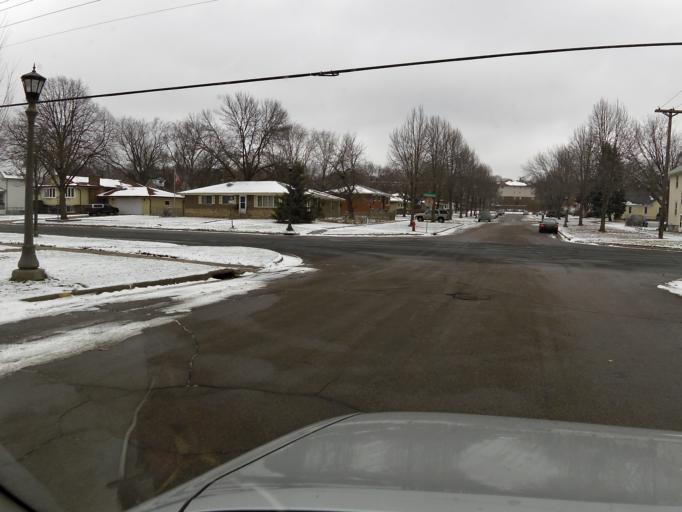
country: US
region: Minnesota
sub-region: Dakota County
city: West Saint Paul
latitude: 44.9304
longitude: -93.1257
